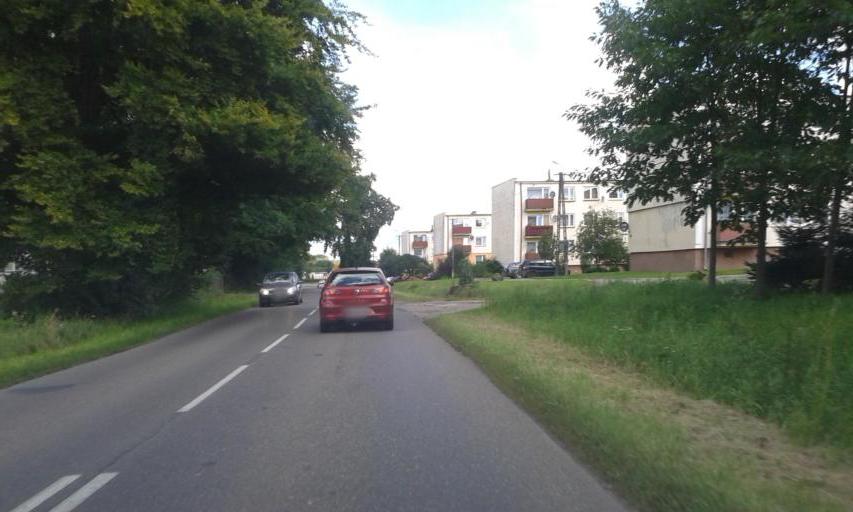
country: PL
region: West Pomeranian Voivodeship
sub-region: Powiat slawienski
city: Slawno
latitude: 54.2728
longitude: 16.6726
